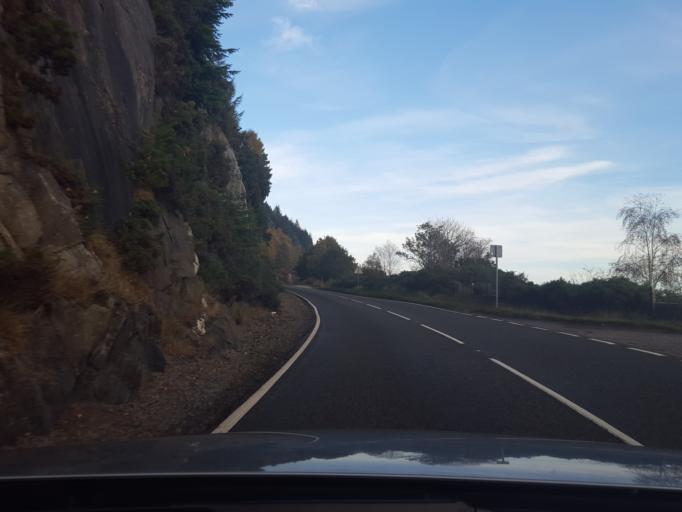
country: GB
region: Scotland
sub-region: Highland
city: Beauly
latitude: 57.3442
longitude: -4.4211
